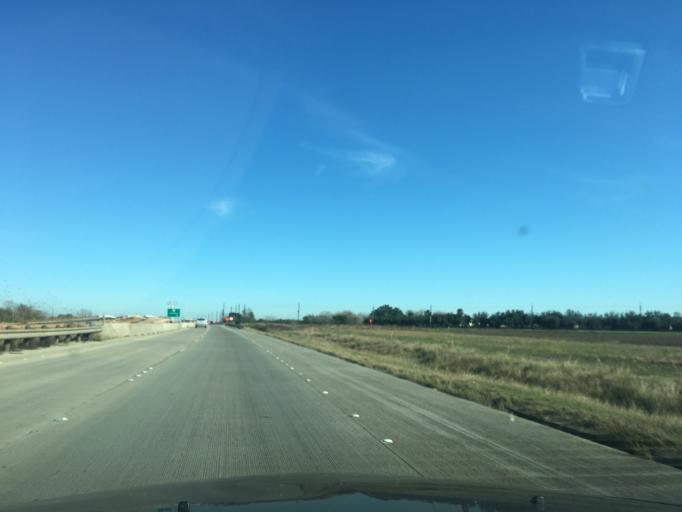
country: US
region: Texas
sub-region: Fort Bend County
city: Rosenberg
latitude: 29.5316
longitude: -95.8252
